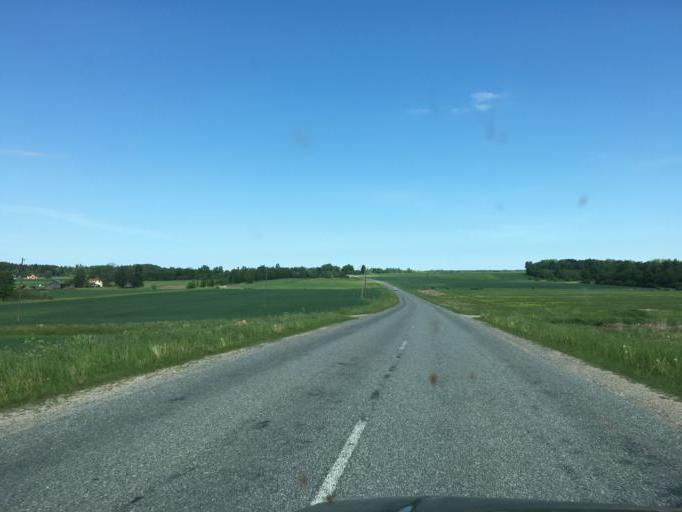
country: LV
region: Talsu Rajons
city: Valdemarpils
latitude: 57.3652
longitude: 22.4887
